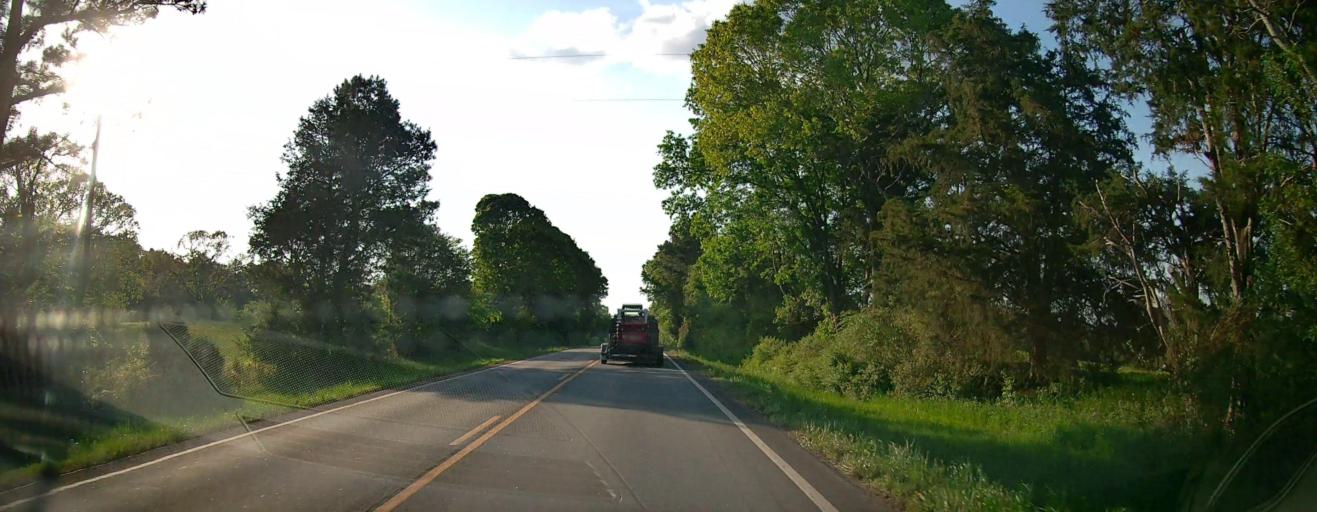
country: US
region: Georgia
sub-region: Putnam County
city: Eatonton
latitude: 33.3299
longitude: -83.5034
